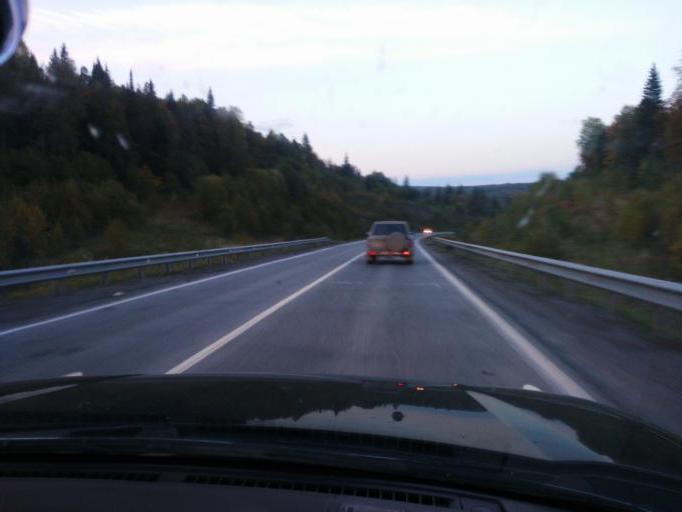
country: RU
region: Perm
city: Sylva
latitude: 58.2963
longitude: 56.7584
